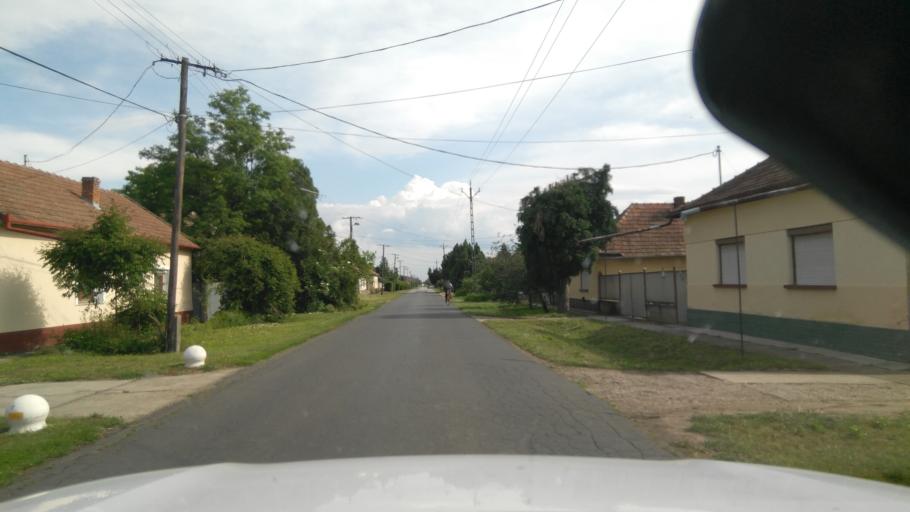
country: HU
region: Bekes
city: Ujkigyos
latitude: 46.5923
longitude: 21.0337
